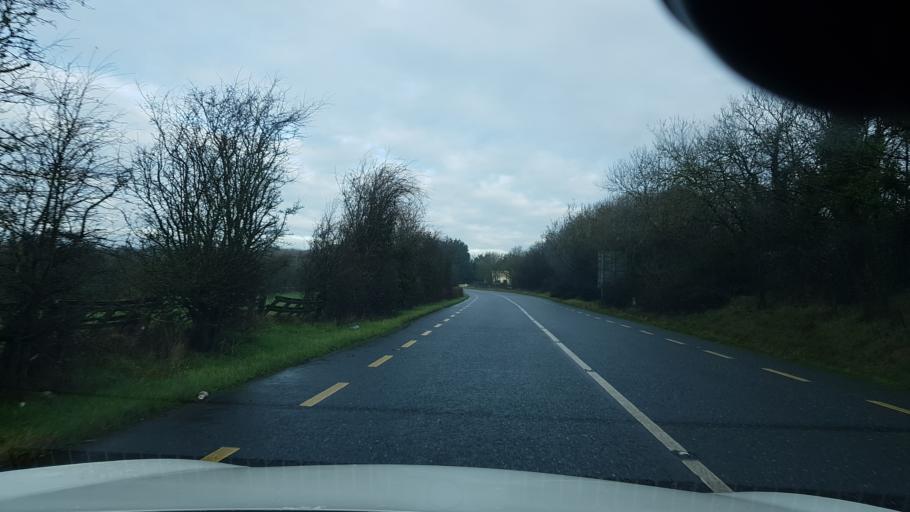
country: IE
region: Leinster
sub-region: An Mhi
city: Ratoath
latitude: 53.4568
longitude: -6.4825
